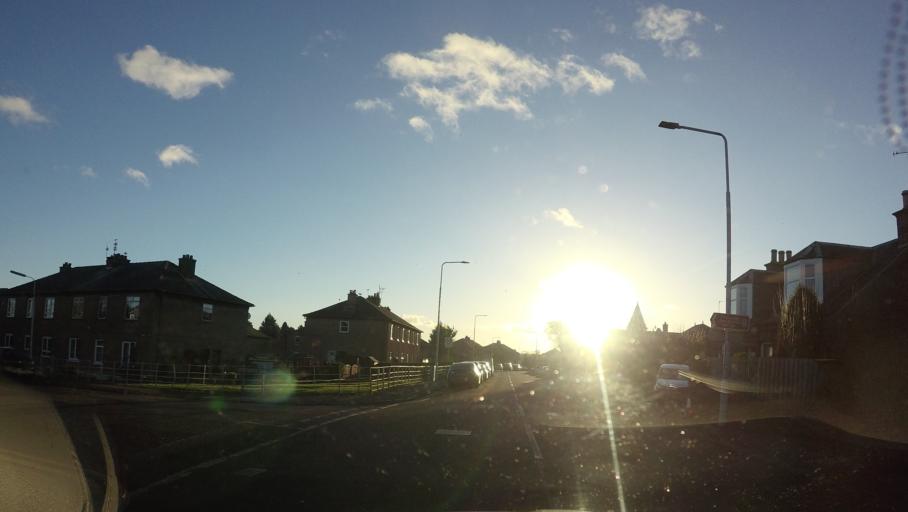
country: GB
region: Scotland
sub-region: Fife
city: Tayport
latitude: 56.4449
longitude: -2.8814
